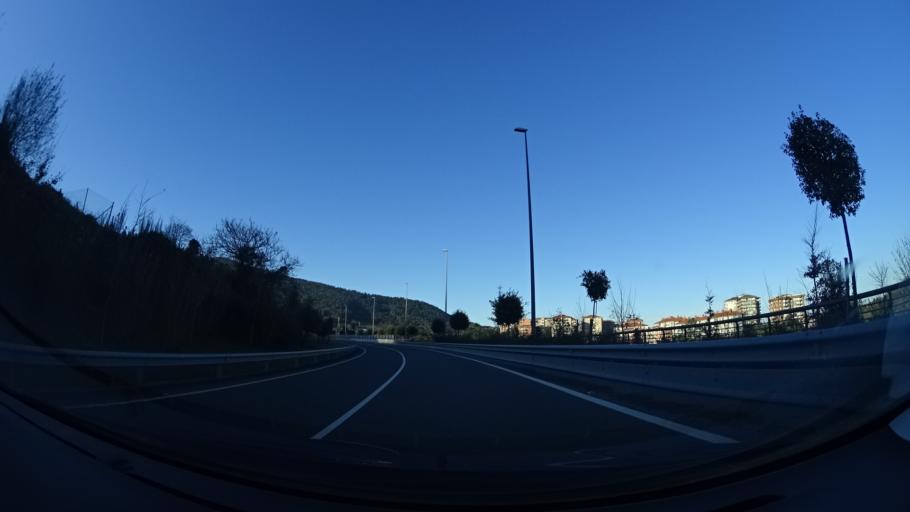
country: ES
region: Basque Country
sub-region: Bizkaia
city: Lekeitio
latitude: 43.3577
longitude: -2.5086
